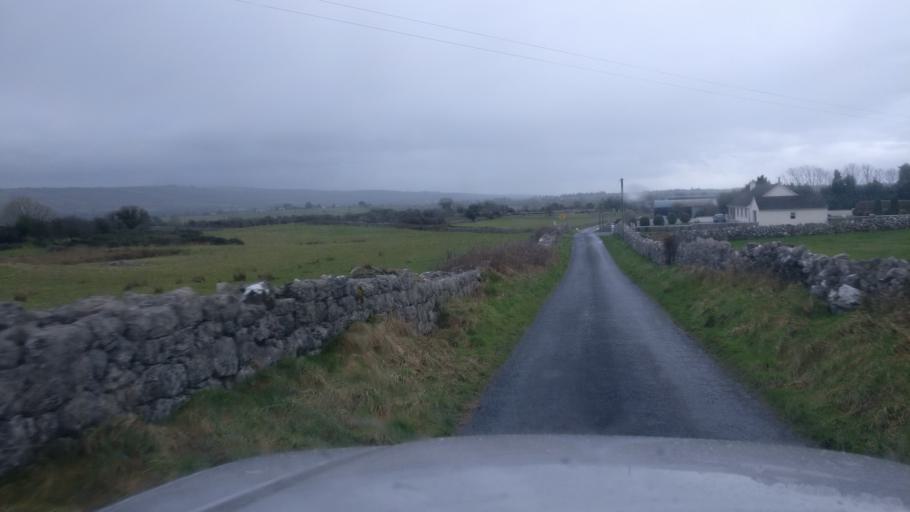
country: IE
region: Connaught
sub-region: County Galway
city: Loughrea
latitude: 53.1977
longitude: -8.6824
